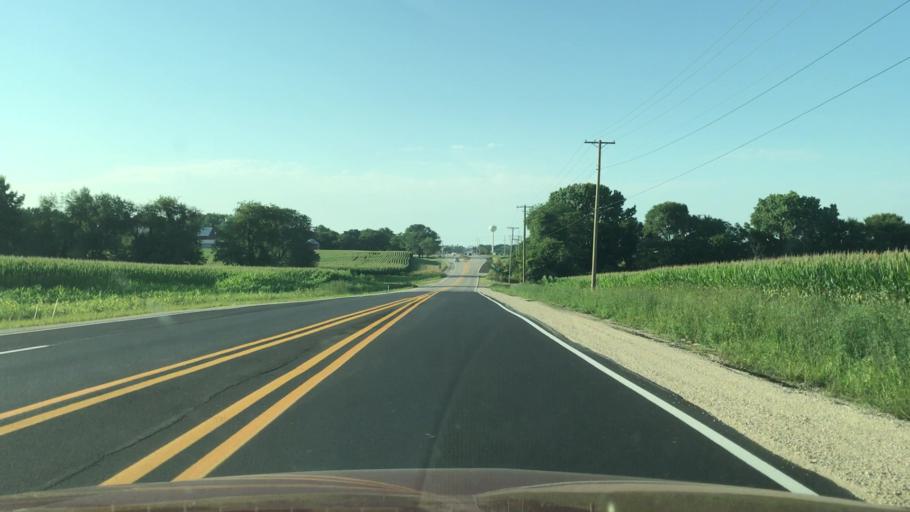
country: US
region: Illinois
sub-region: Winnebago County
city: Cherry Valley
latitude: 42.2340
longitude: -88.9795
